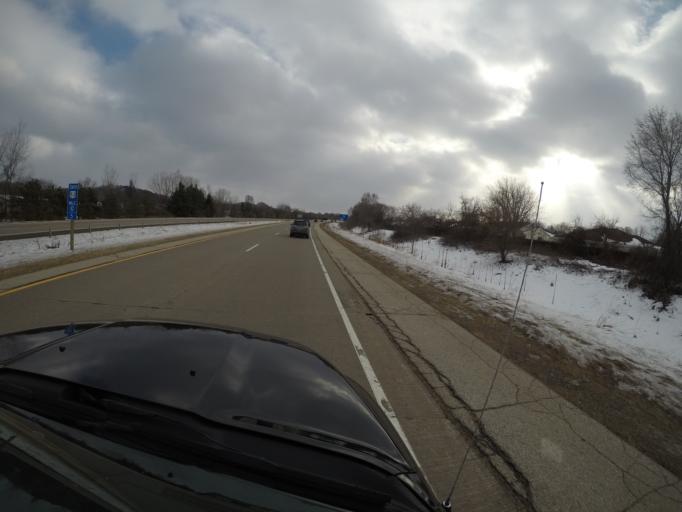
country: US
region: Wisconsin
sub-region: La Crosse County
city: Holmen
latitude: 43.9337
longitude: -91.2454
